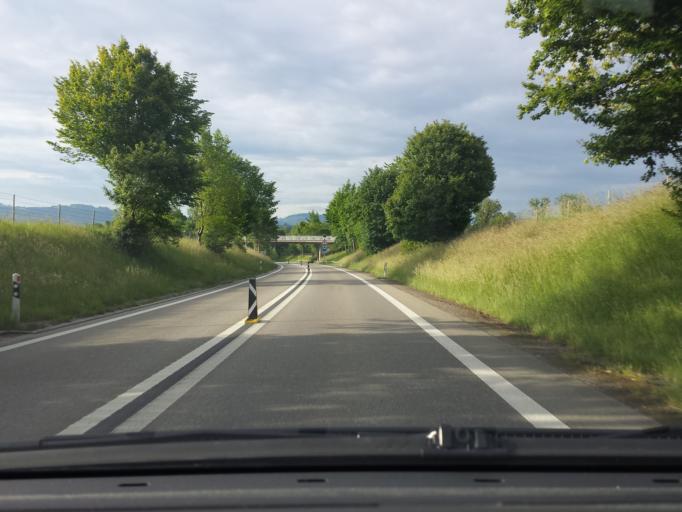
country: CH
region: Thurgau
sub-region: Arbon District
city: Roggwil
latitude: 47.5113
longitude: 9.4041
